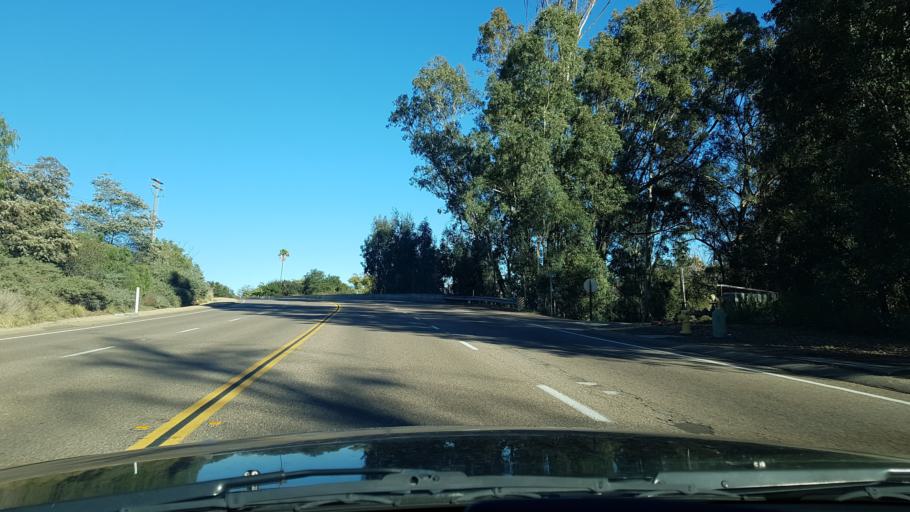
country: US
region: California
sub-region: San Diego County
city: Hidden Meadows
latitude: 33.2042
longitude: -117.1133
